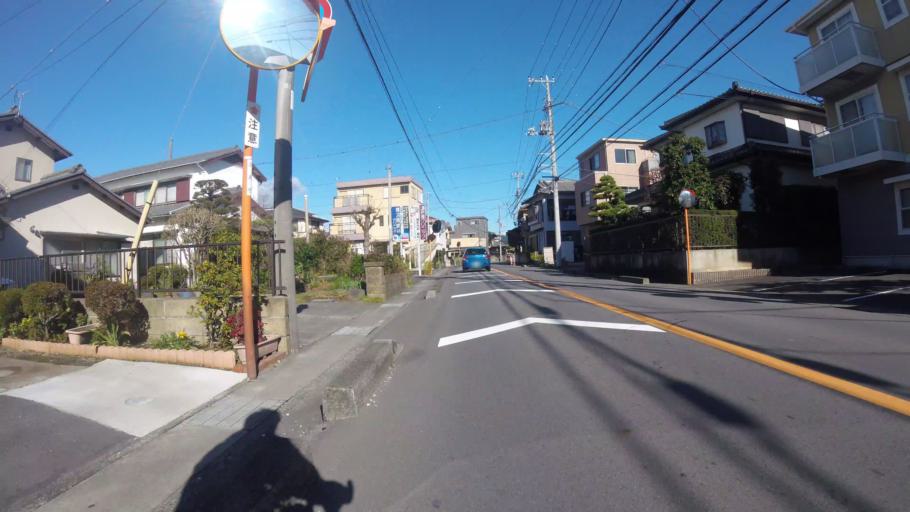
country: JP
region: Shizuoka
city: Numazu
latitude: 35.1076
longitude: 138.8787
